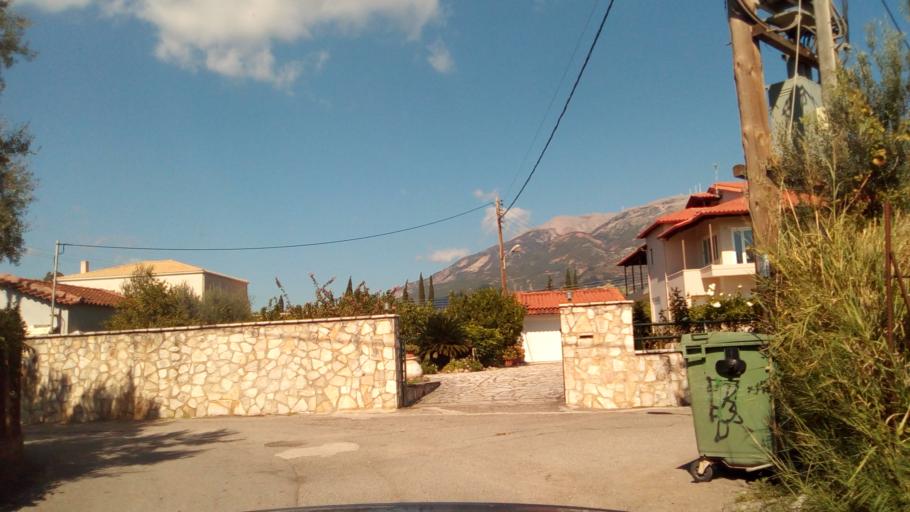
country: GR
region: West Greece
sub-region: Nomos Aitolias kai Akarnanias
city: Nafpaktos
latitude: 38.3877
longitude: 21.8008
